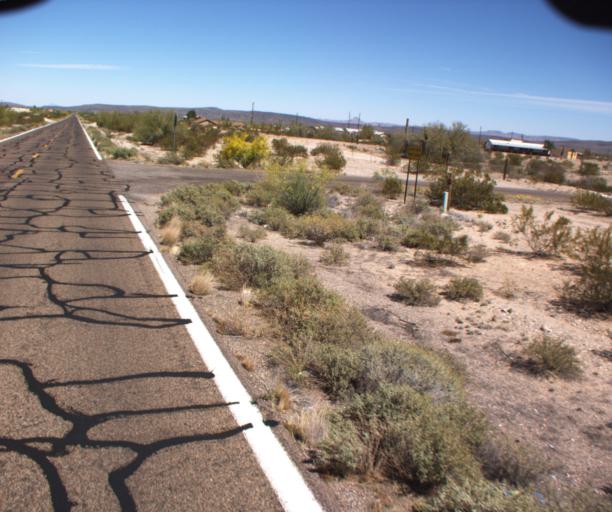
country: US
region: Arizona
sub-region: Pima County
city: Ajo
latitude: 32.4143
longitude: -112.8716
